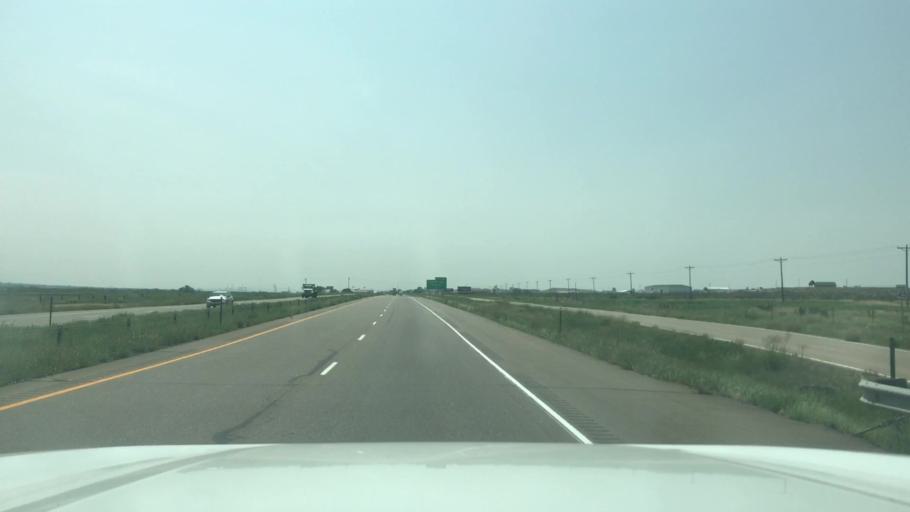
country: US
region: Colorado
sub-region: Pueblo County
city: Pueblo West
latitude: 38.3615
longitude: -104.6209
